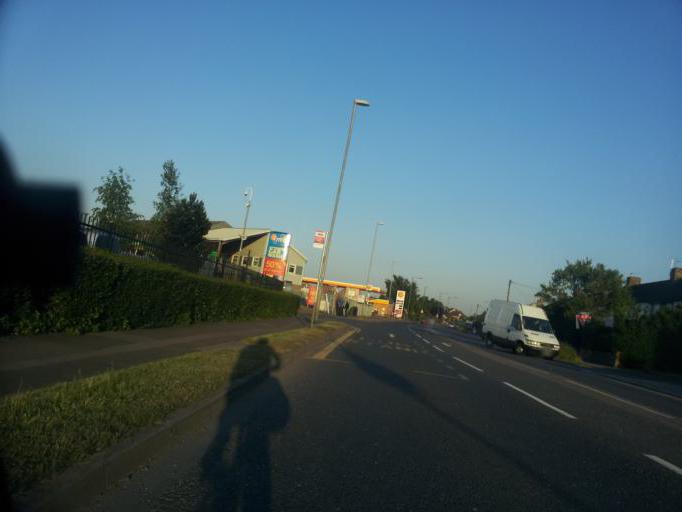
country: GB
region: England
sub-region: Kent
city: Dartford
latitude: 51.4554
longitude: 0.2064
